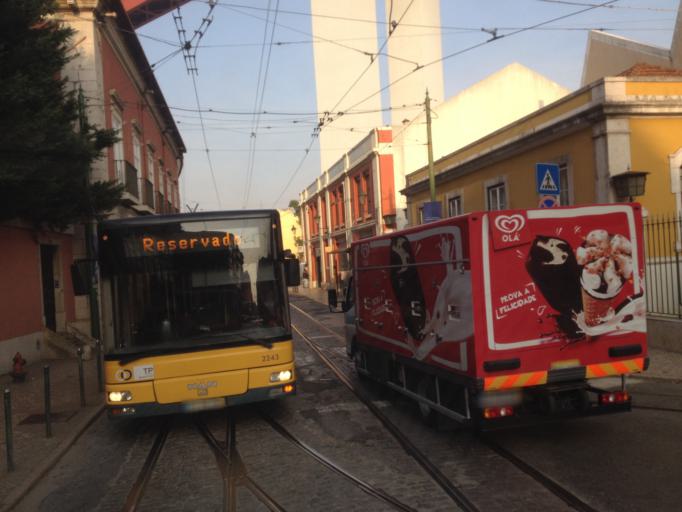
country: PT
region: Setubal
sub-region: Almada
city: Pragal
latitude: 38.7027
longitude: -9.1803
